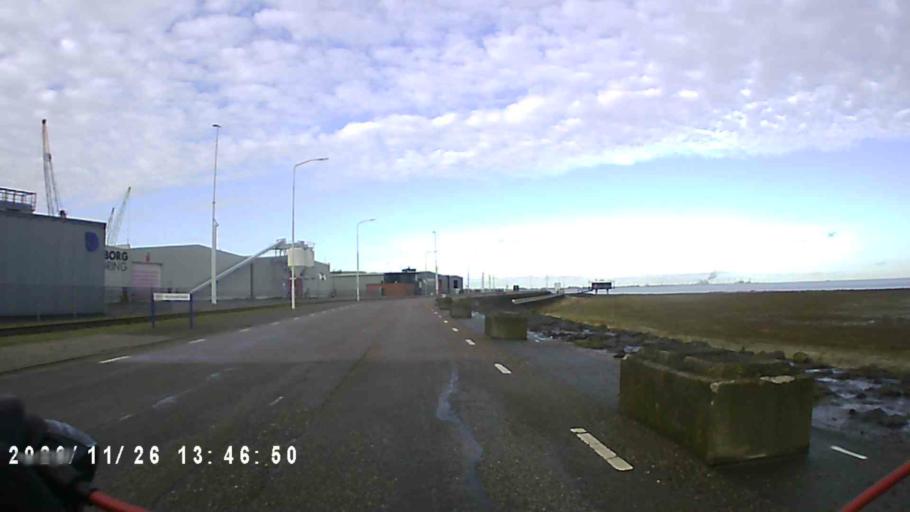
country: NL
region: Groningen
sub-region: Gemeente Delfzijl
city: Delfzijl
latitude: 53.3321
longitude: 6.9386
